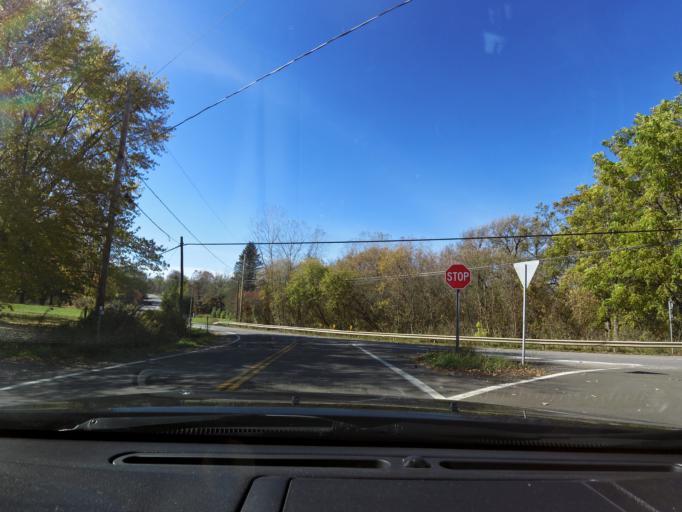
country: US
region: New York
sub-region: Wyoming County
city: Castile
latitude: 42.5928
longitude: -78.1032
